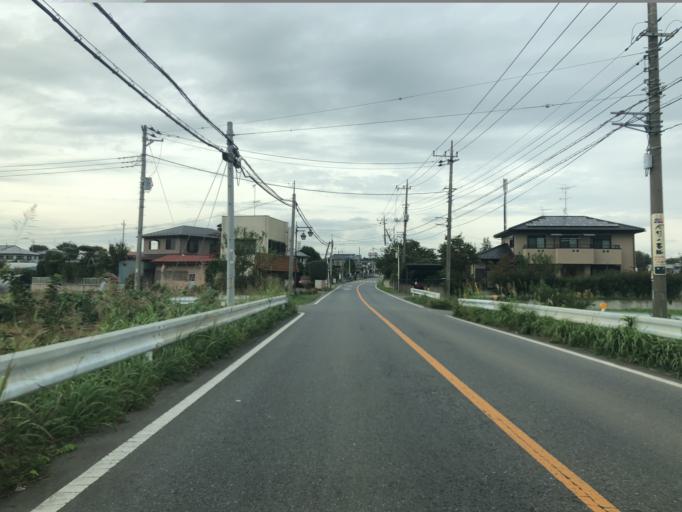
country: JP
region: Saitama
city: Fukiage-fujimi
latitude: 36.0574
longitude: 139.4074
